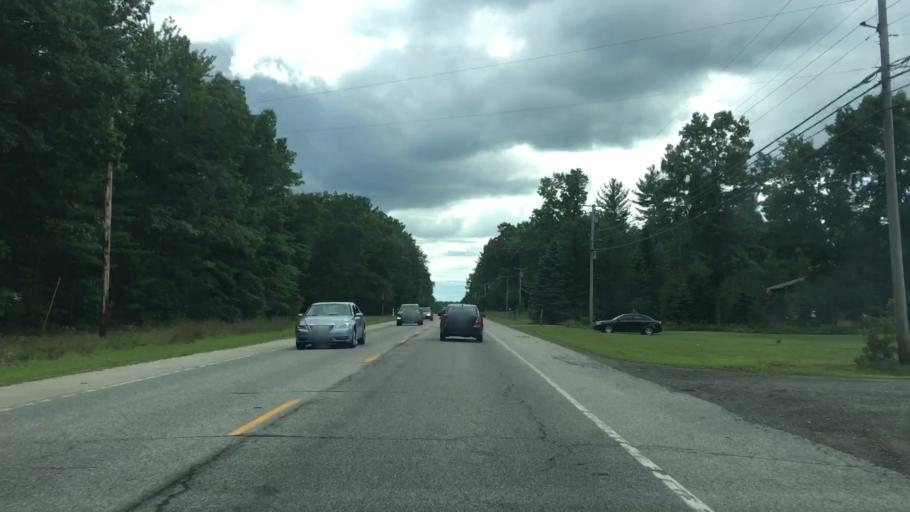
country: US
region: Maine
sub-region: York County
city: North Berwick
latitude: 43.3319
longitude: -70.7351
